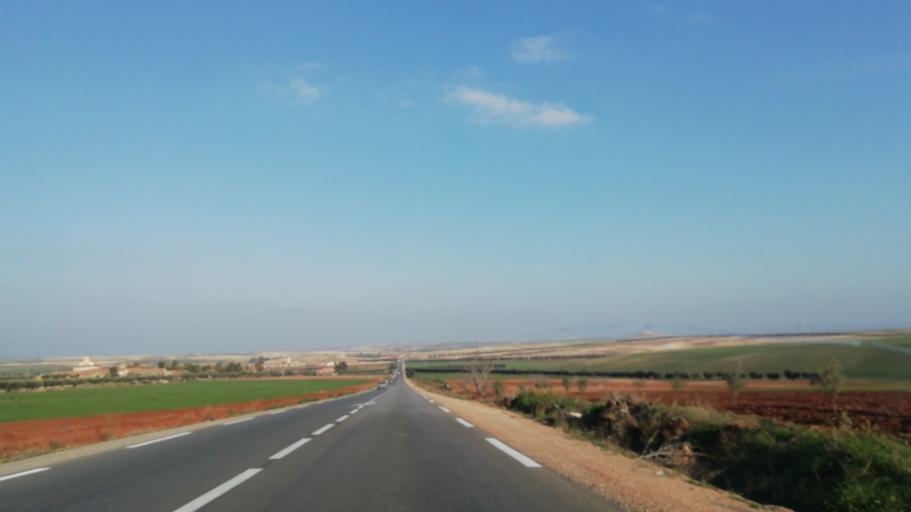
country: DZ
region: Sidi Bel Abbes
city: Sidi Bel Abbes
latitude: 35.1740
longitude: -0.8288
